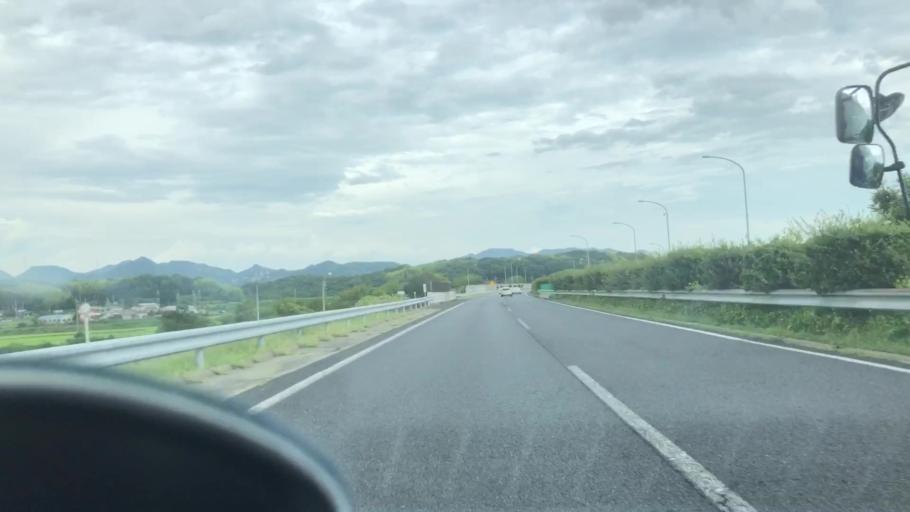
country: JP
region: Hyogo
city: Yashiro
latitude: 34.9308
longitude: 134.9629
